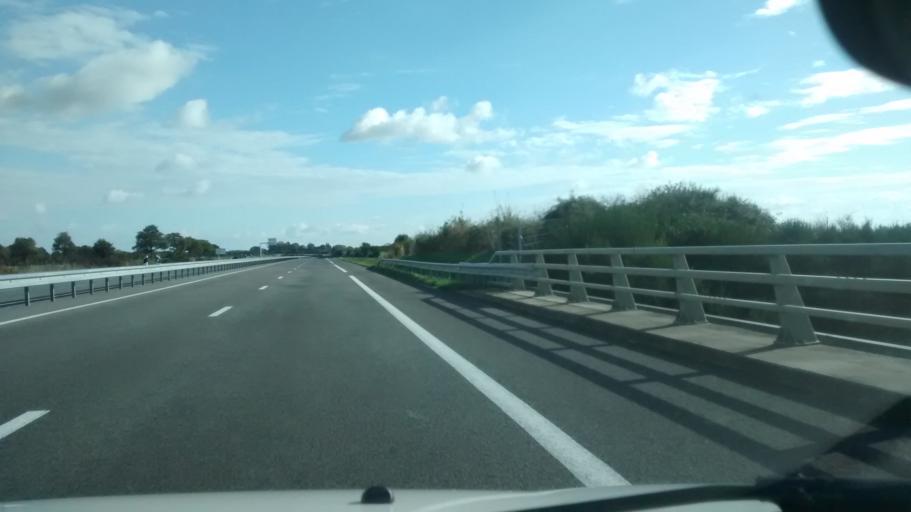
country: FR
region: Pays de la Loire
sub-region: Departement de Maine-et-Loire
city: Pouance
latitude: 47.7299
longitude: -1.1080
